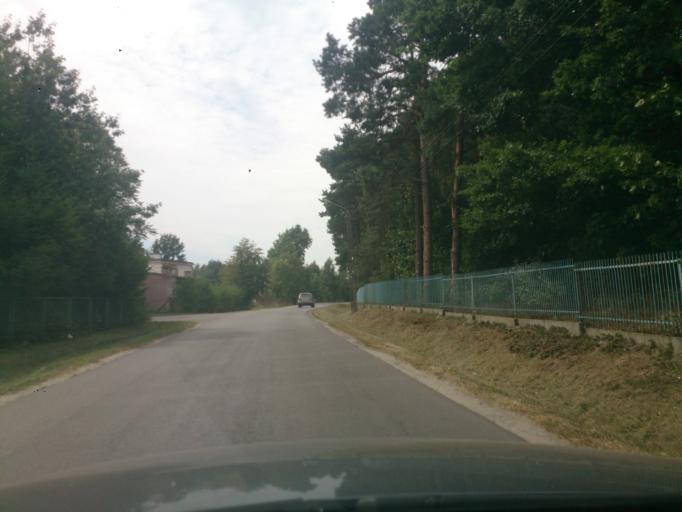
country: PL
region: Subcarpathian Voivodeship
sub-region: Powiat kolbuszowski
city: Kolbuszowa
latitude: 50.2345
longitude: 21.7675
